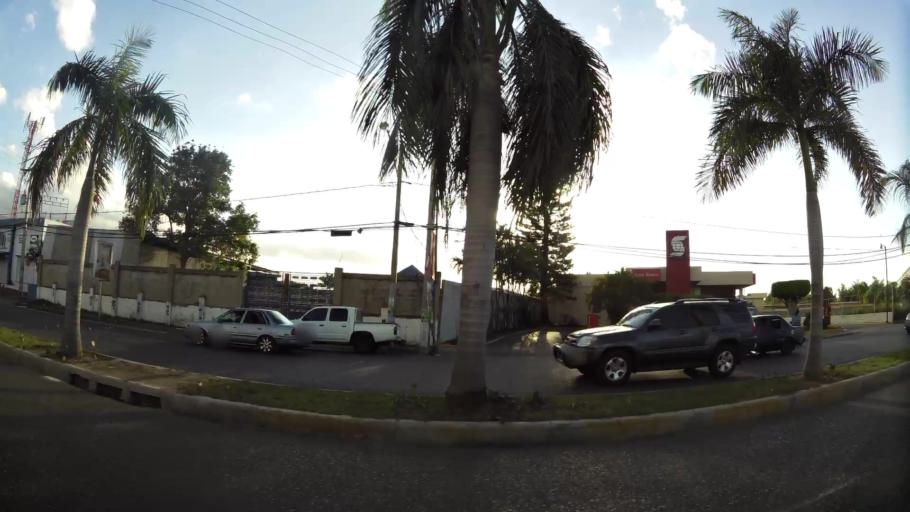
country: DO
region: Santiago
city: Santiago de los Caballeros
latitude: 19.4829
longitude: -70.7189
